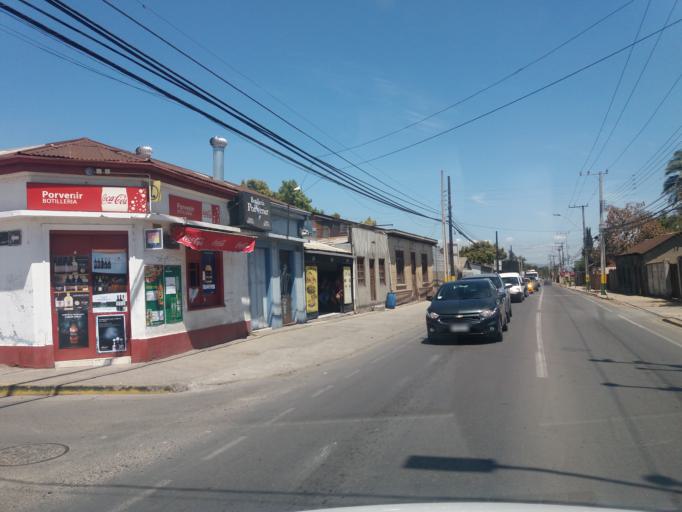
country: CL
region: Valparaiso
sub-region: Provincia de Quillota
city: Quillota
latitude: -32.8545
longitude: -71.2346
